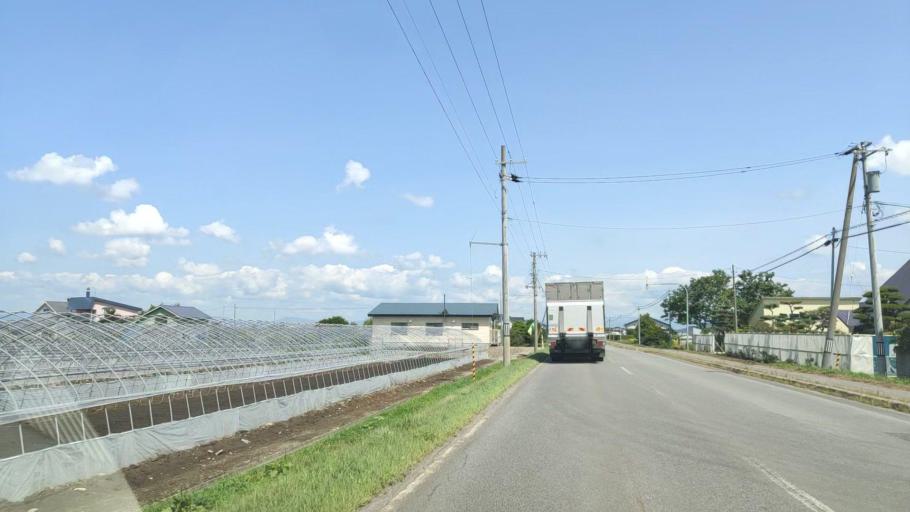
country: JP
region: Hokkaido
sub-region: Asahikawa-shi
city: Asahikawa
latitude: 43.7175
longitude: 142.4575
